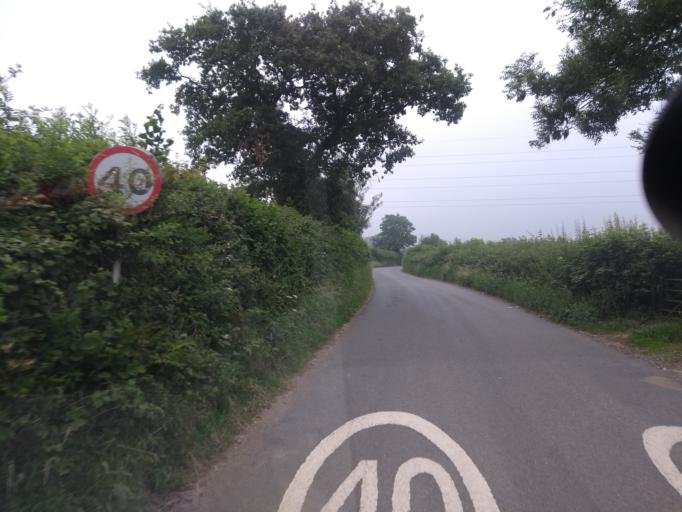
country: GB
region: England
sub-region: Somerset
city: Crewkerne
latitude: 50.8399
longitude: -2.8215
